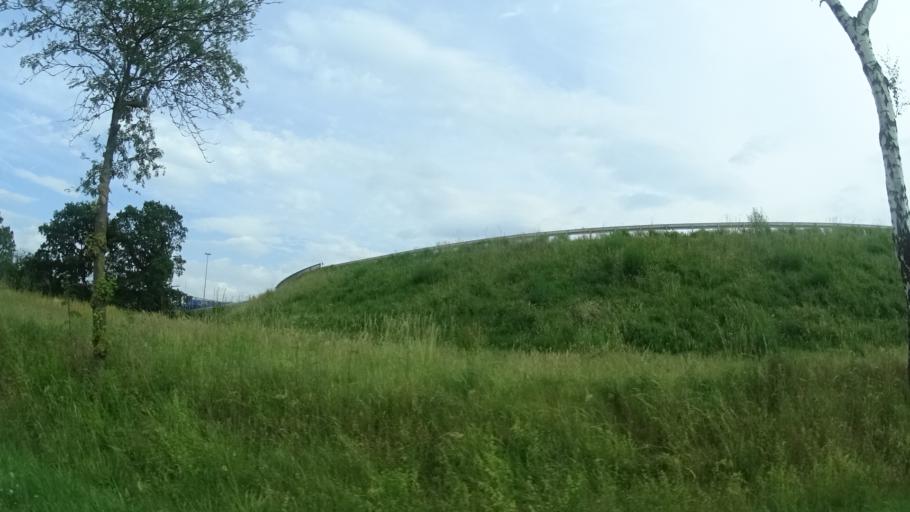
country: DE
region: Hesse
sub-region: Regierungsbezirk Kassel
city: Volkmarsen
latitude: 51.3998
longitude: 9.0975
